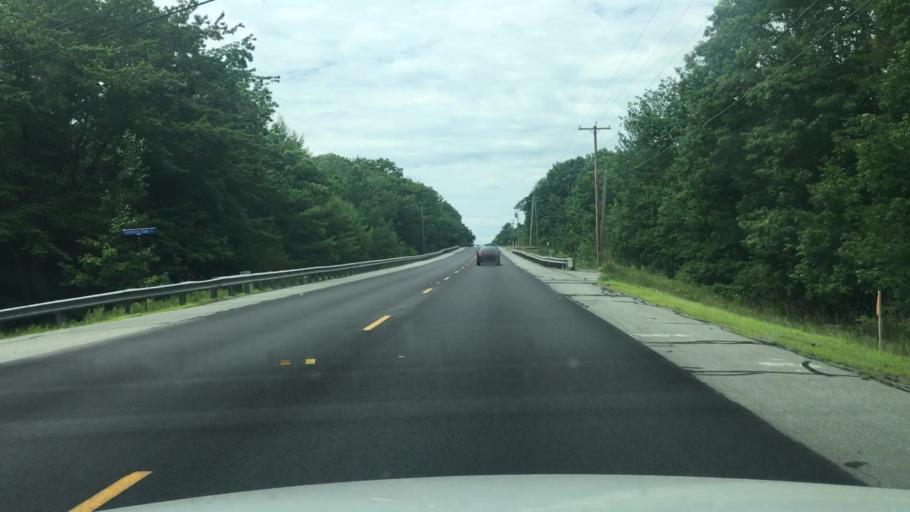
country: US
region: Maine
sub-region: Waldo County
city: Palermo
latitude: 44.4104
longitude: -69.5030
